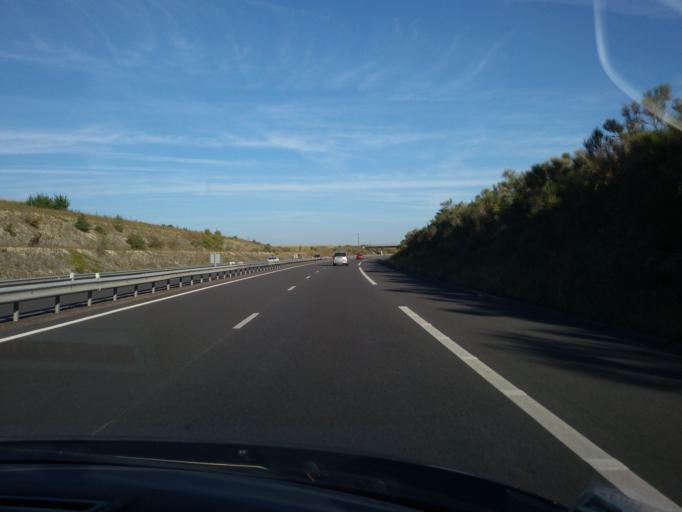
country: FR
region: Centre
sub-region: Departement du Cher
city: Trouy
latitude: 47.0078
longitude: 2.3911
